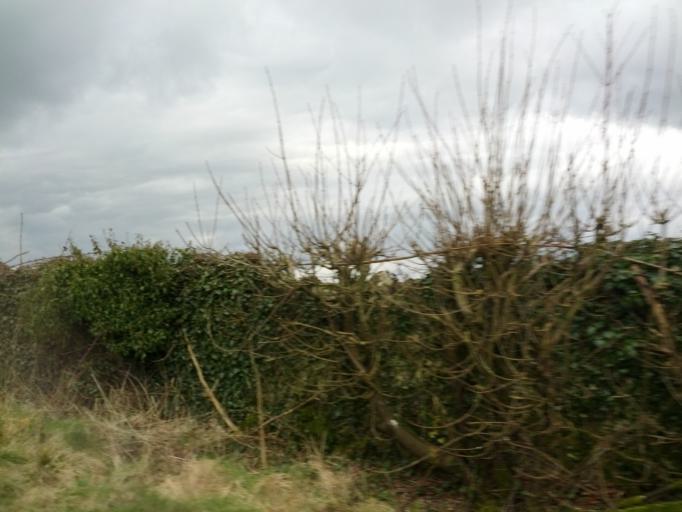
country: IE
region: Connaught
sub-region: County Galway
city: Athenry
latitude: 53.4408
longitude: -8.6365
